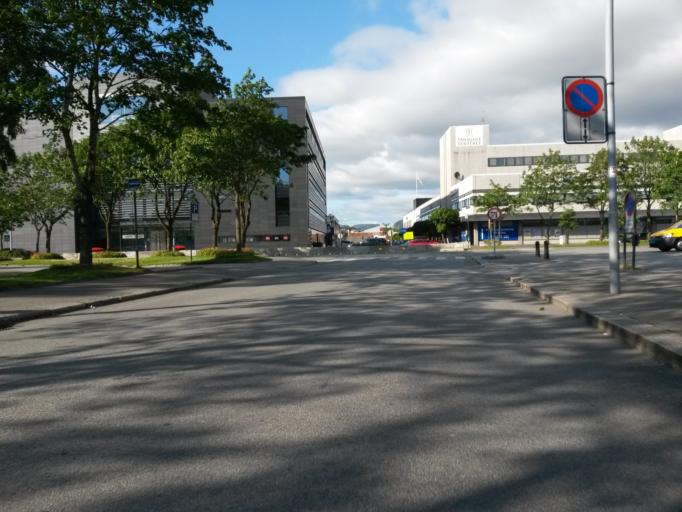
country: NO
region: Rogaland
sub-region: Sandnes
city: Sandnes
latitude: 58.8525
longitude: 5.7389
